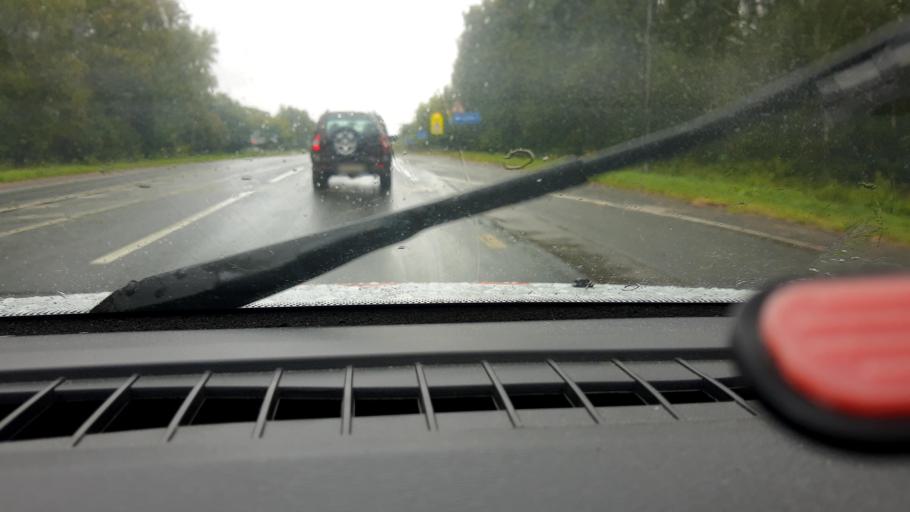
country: RU
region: Nizjnij Novgorod
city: Pamyat' Parizhskoy Kommuny
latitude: 56.0573
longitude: 44.3959
